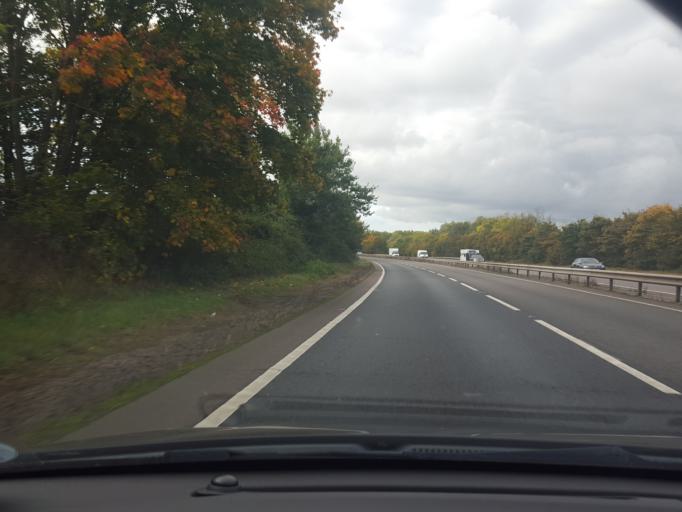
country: GB
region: England
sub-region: Suffolk
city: Thurston
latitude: 52.2374
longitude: 0.8340
